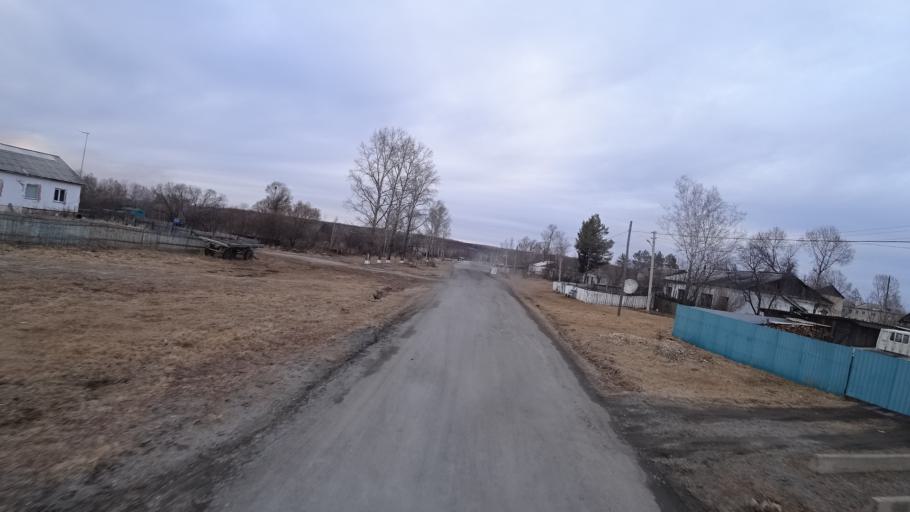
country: RU
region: Amur
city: Bureya
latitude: 50.0171
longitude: 129.7681
